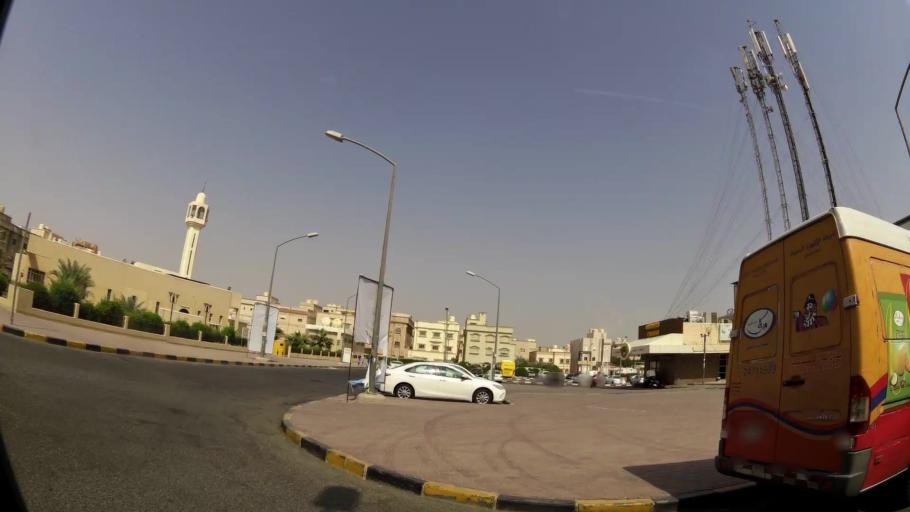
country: KW
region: Muhafazat al Jahra'
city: Al Jahra'
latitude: 29.3032
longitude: 47.7072
